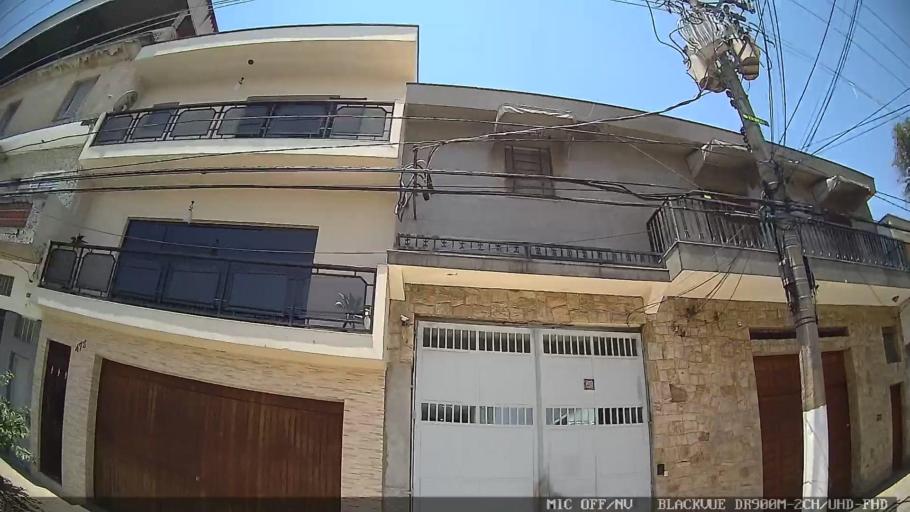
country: BR
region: Sao Paulo
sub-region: Sao Caetano Do Sul
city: Sao Caetano do Sul
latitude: -23.5681
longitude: -46.5719
